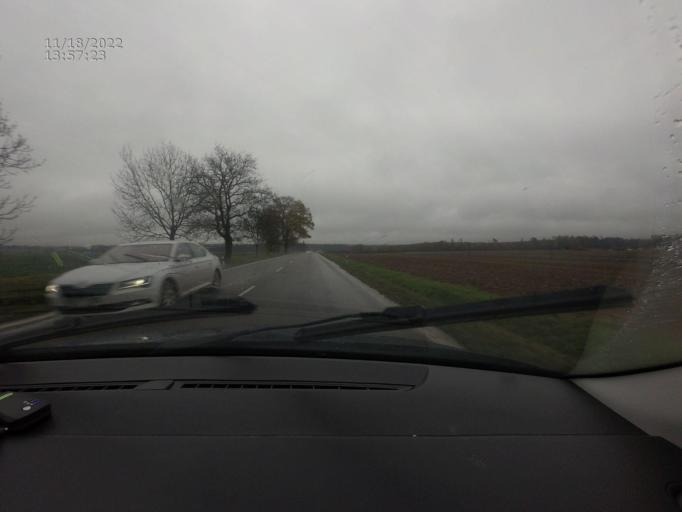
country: CZ
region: Jihocesky
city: Sedlice
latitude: 49.3685
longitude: 13.9588
